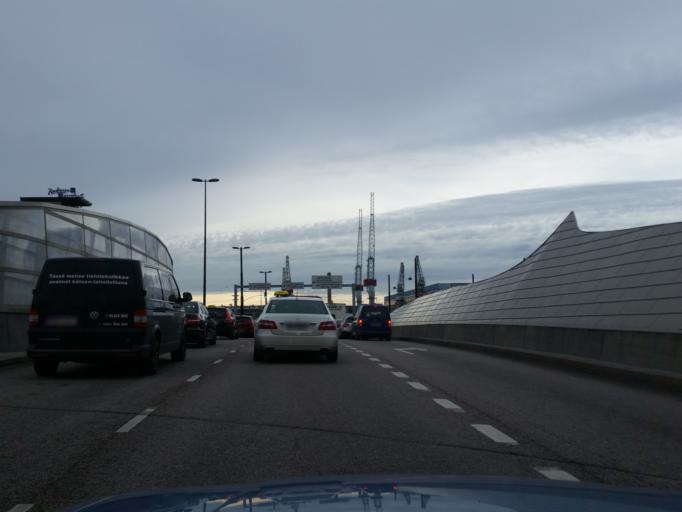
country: FI
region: Uusimaa
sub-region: Helsinki
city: Helsinki
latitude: 60.1630
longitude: 24.9216
